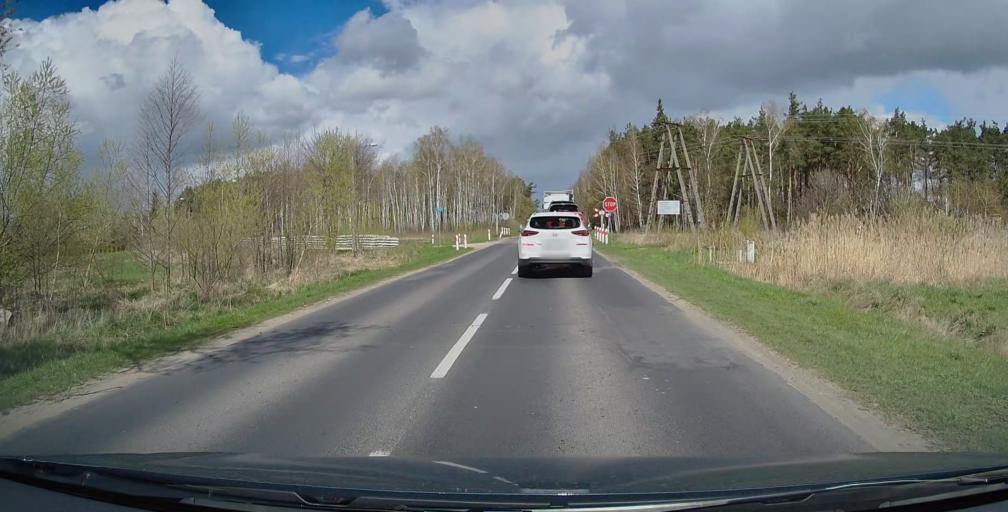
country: PL
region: Masovian Voivodeship
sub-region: Ostroleka
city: Ostroleka
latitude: 53.0559
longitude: 21.5861
